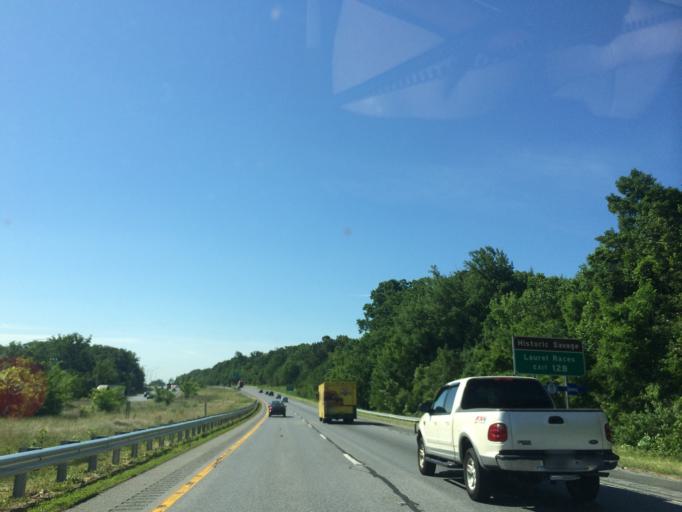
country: US
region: Maryland
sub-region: Howard County
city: Savage
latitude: 39.1467
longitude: -76.8221
